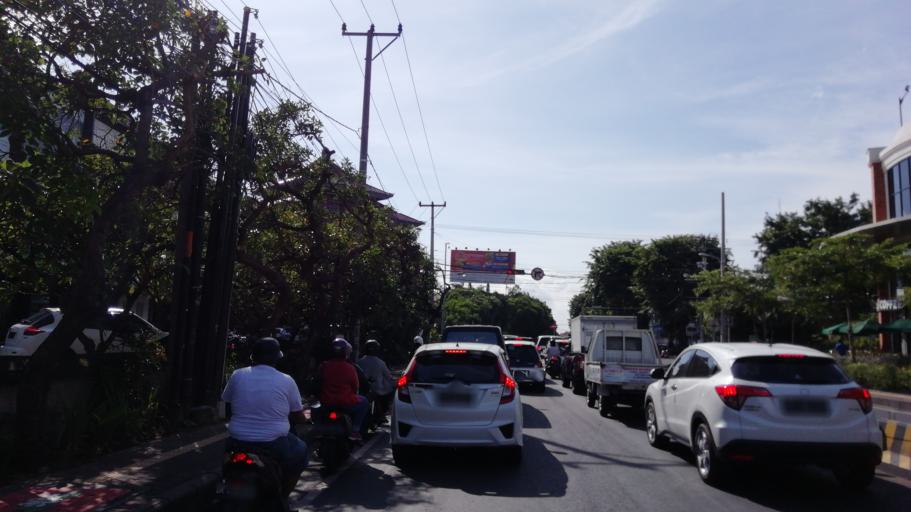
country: ID
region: Bali
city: Denpasar
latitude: -8.6695
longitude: 115.2149
